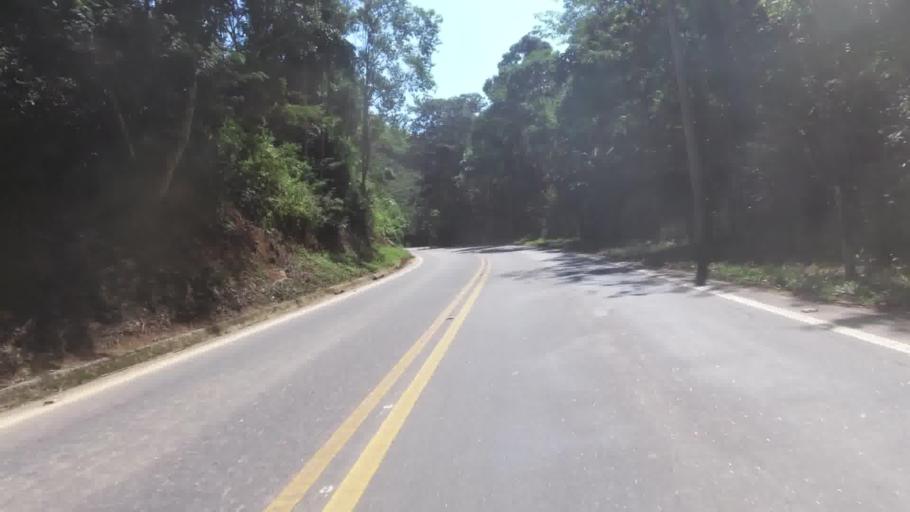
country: BR
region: Espirito Santo
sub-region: Marechal Floriano
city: Marechal Floriano
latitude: -20.4317
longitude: -40.7766
